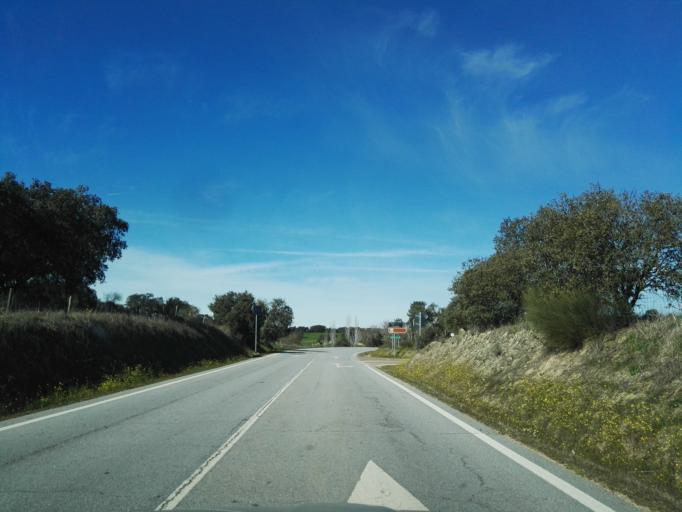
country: PT
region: Portalegre
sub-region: Arronches
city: Arronches
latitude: 39.0648
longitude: -7.2752
